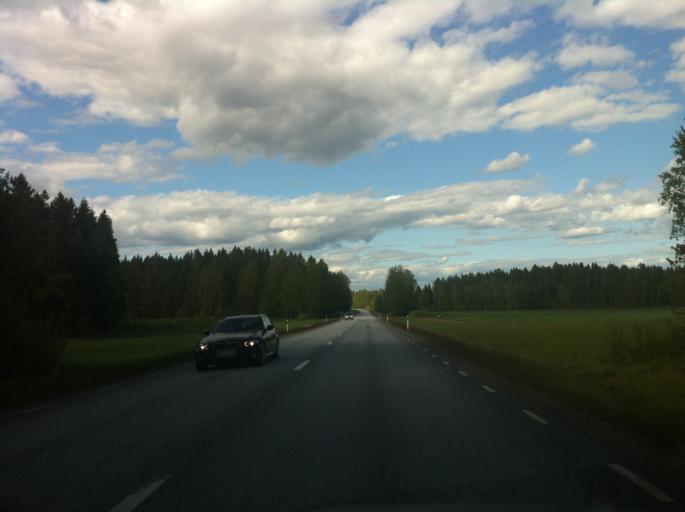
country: SE
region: Vaermland
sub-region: Storfors Kommun
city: Storfors
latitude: 59.4558
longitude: 14.2466
